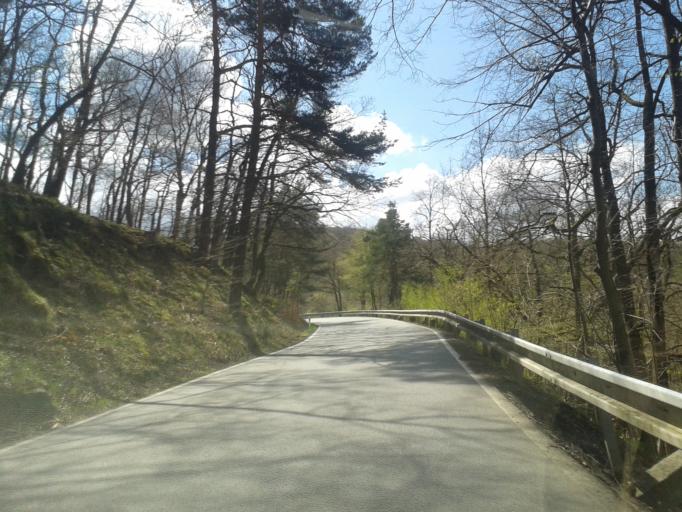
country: CZ
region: Central Bohemia
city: Revnice
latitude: 49.8959
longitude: 14.2388
